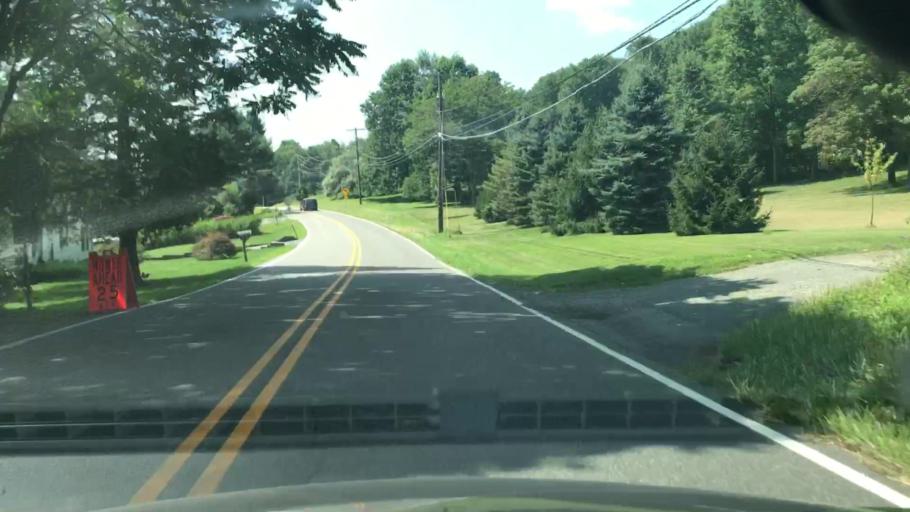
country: US
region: New Jersey
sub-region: Hunterdon County
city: Milford
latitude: 40.6199
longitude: -75.0436
